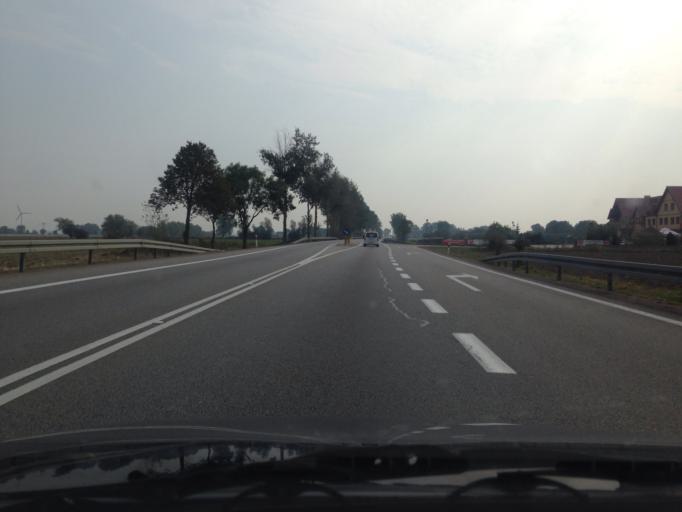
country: PL
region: Pomeranian Voivodeship
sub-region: Powiat nowodworski
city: Ostaszewo
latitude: 54.2539
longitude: 18.9638
